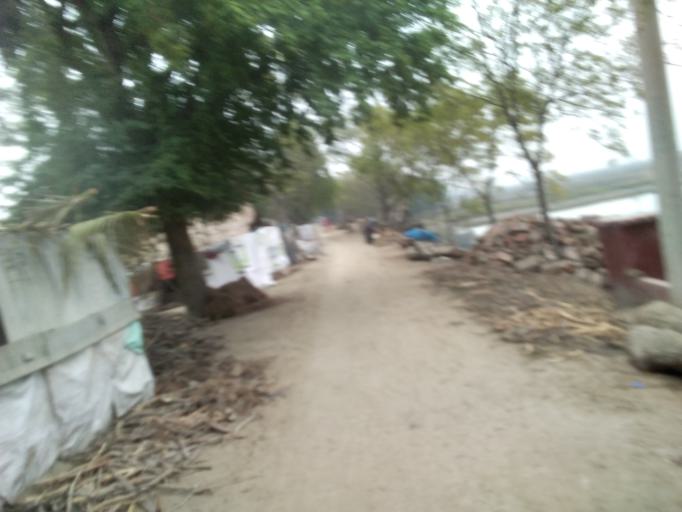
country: BD
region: Khulna
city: Satkhira
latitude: 22.5711
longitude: 89.0779
